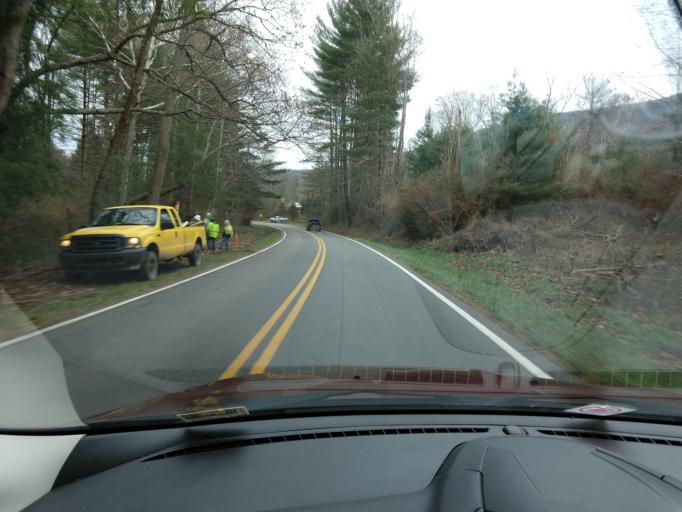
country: US
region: Virginia
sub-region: City of Covington
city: Covington
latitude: 37.7574
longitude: -80.1300
